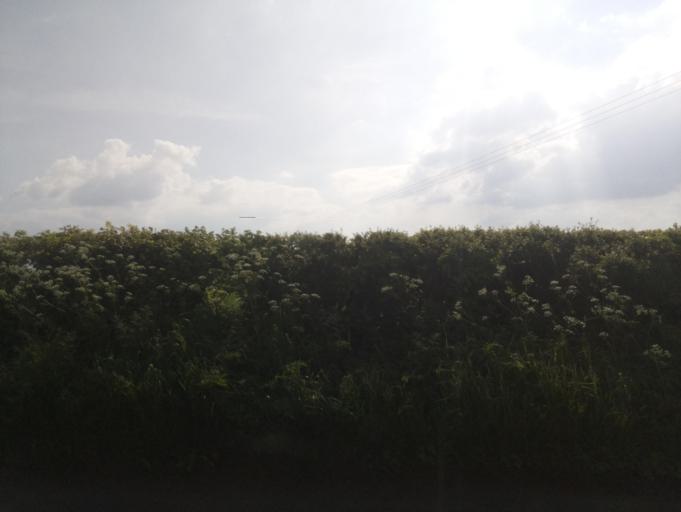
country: GB
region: England
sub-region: Wiltshire
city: Norton
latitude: 51.5523
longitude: -2.1538
